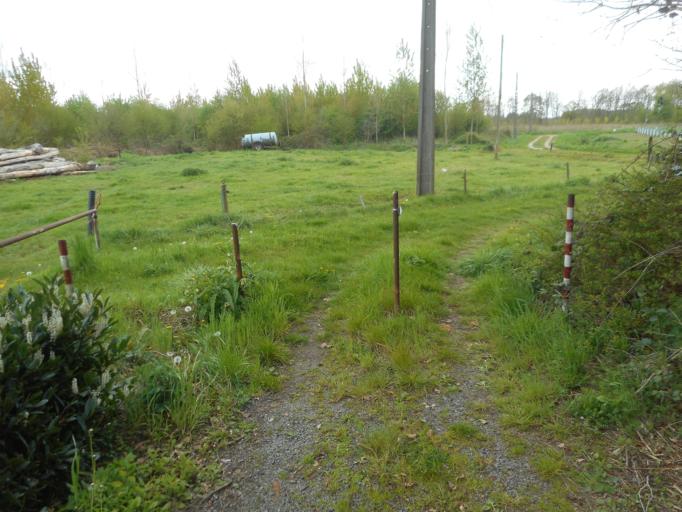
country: BE
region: Flanders
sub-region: Provincie Antwerpen
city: Lier
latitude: 51.0923
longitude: 4.5788
